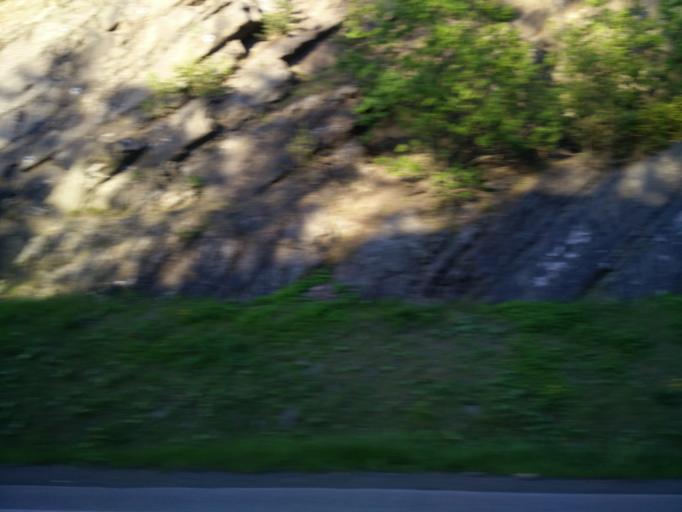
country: NO
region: Buskerud
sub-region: Hole
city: Vik
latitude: 60.0095
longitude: 10.2710
